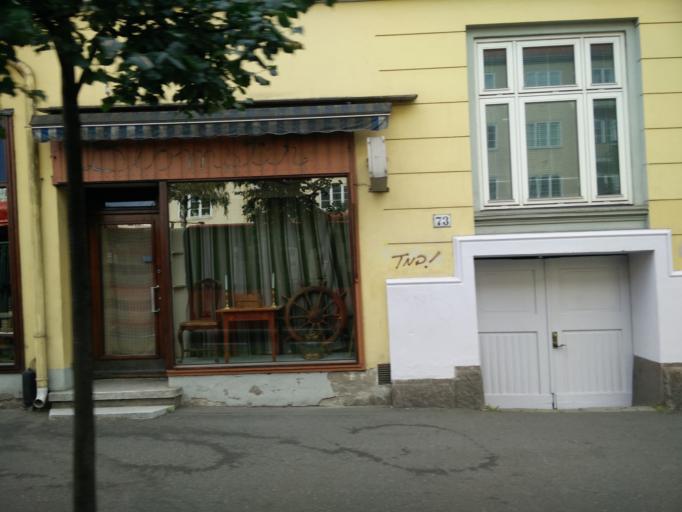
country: NO
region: Oslo
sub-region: Oslo
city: Oslo
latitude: 59.9308
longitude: 10.7203
